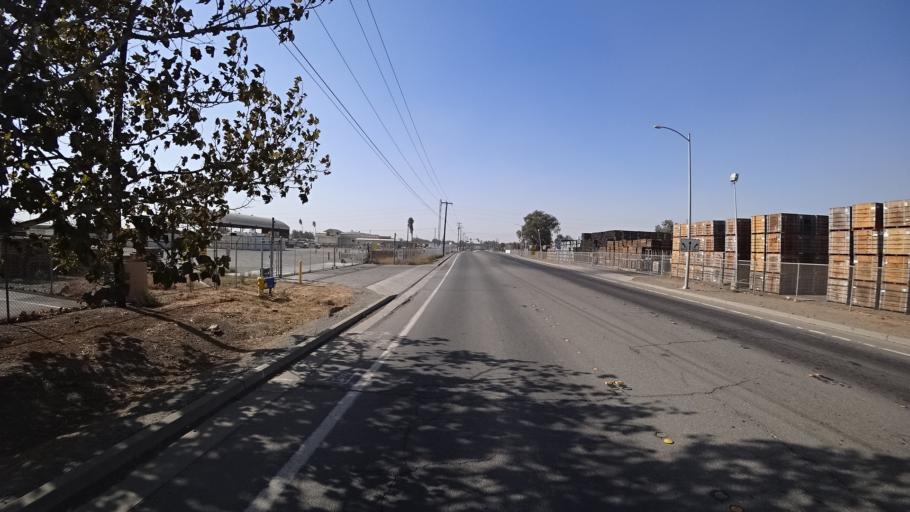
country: US
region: California
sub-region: Yolo County
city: Woodland
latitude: 38.6844
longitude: -121.7444
